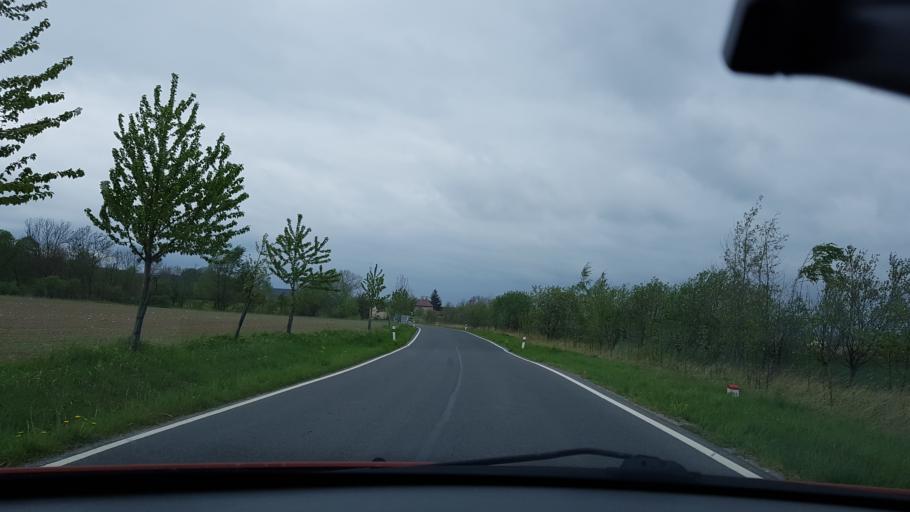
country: PL
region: Opole Voivodeship
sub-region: Powiat nyski
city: Kamienica
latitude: 50.4215
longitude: 16.9711
